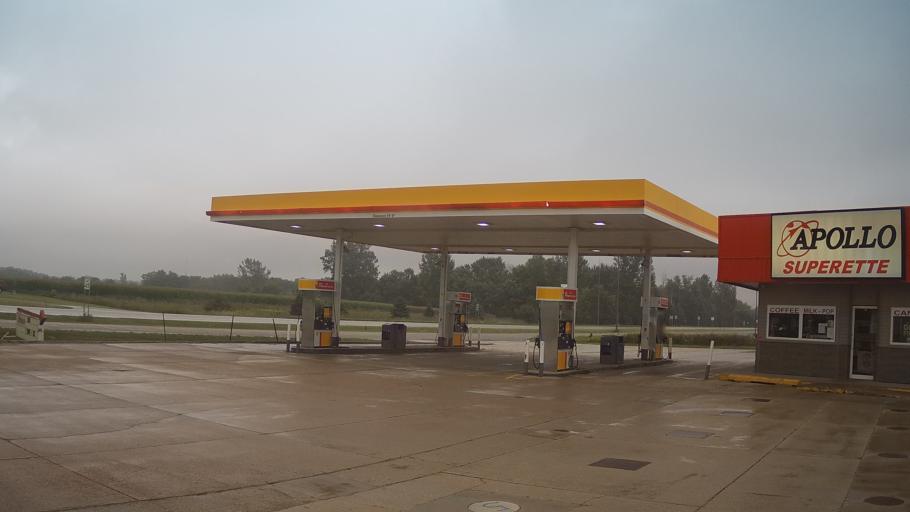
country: US
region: Minnesota
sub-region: Mower County
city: Austin
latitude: 43.6663
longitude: -93.0173
